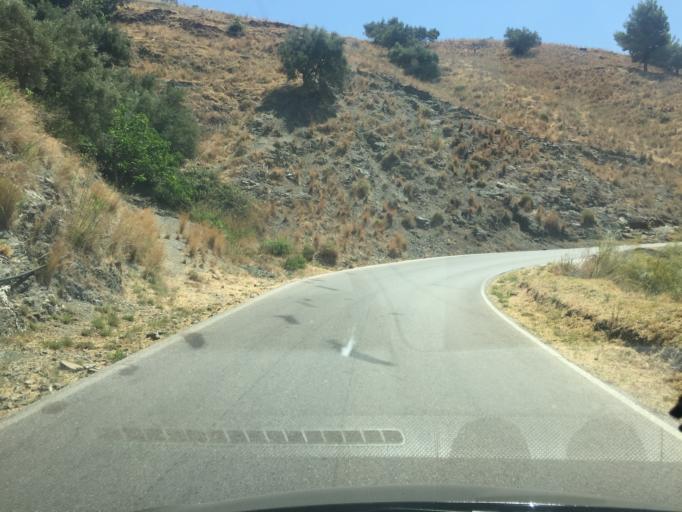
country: ES
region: Andalusia
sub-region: Provincia de Malaga
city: Frigiliana
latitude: 36.8049
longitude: -3.9202
